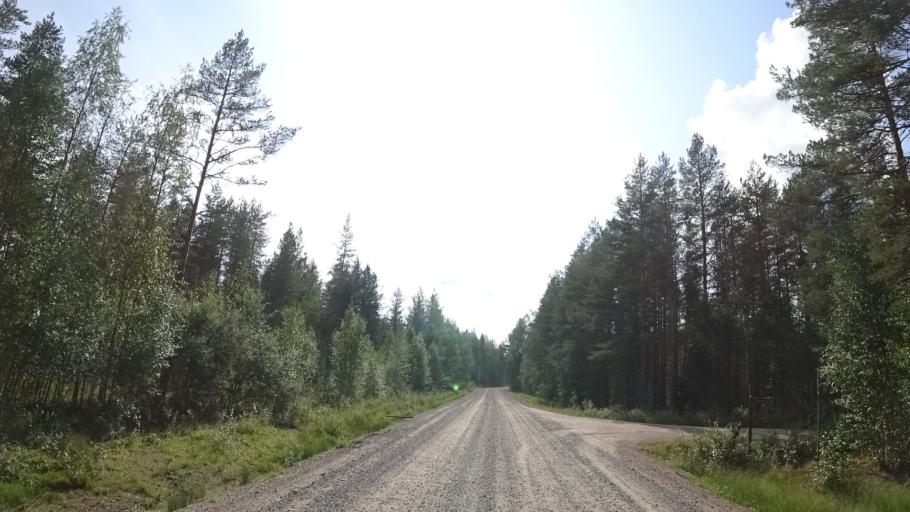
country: FI
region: North Karelia
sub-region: Pielisen Karjala
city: Lieksa
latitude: 63.5661
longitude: 30.0825
